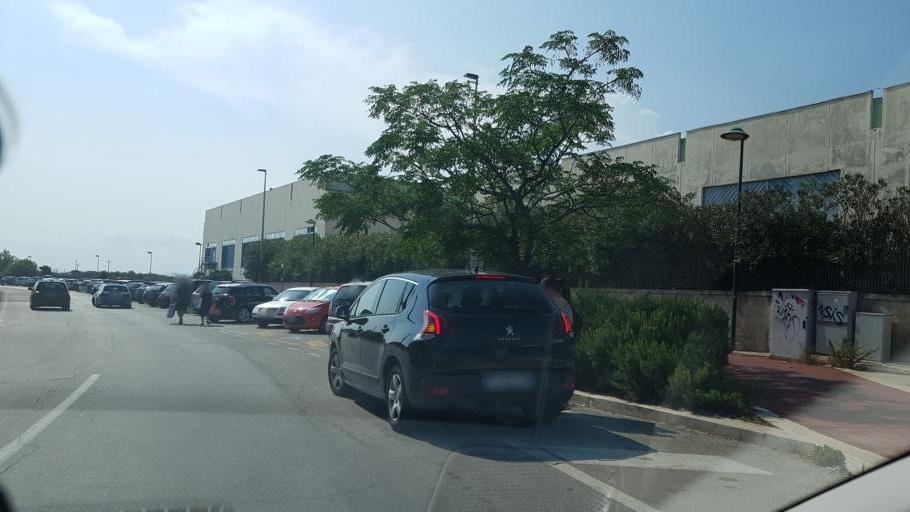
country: IT
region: Apulia
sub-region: Provincia di Bari
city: Monopoli
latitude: 40.9396
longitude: 17.3155
